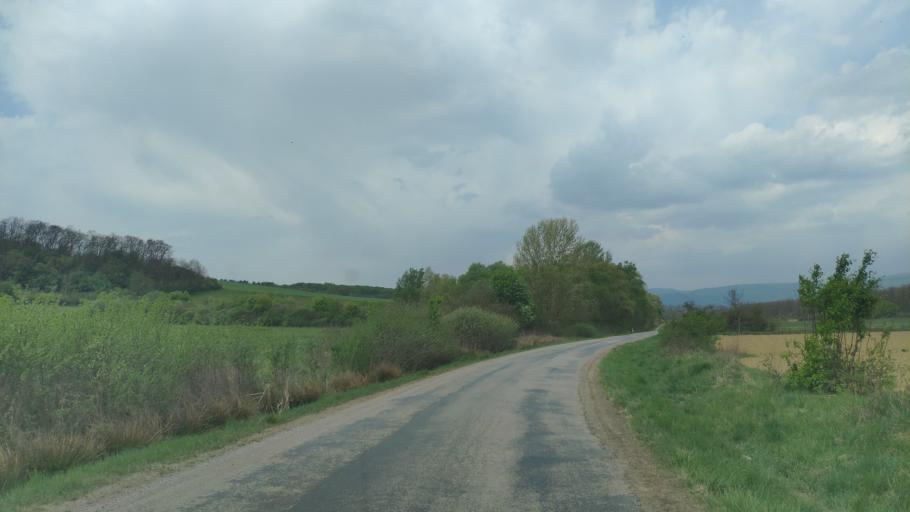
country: SK
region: Kosicky
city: Moldava nad Bodvou
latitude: 48.5599
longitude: 20.9559
